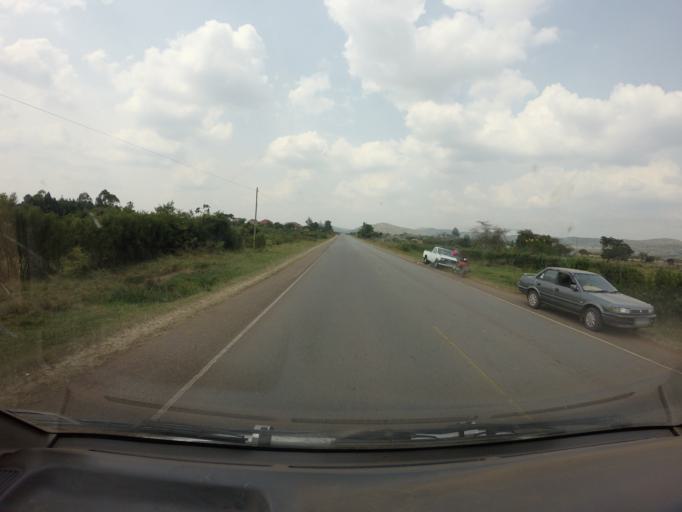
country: UG
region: Central Region
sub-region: Lyantonde District
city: Lyantonde
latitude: -0.3998
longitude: 31.1674
